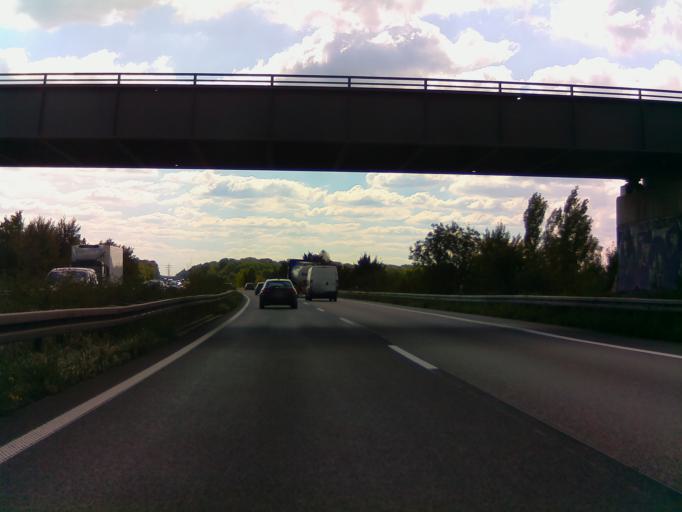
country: DE
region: Hesse
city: Gernsheim
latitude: 49.7656
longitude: 8.5442
